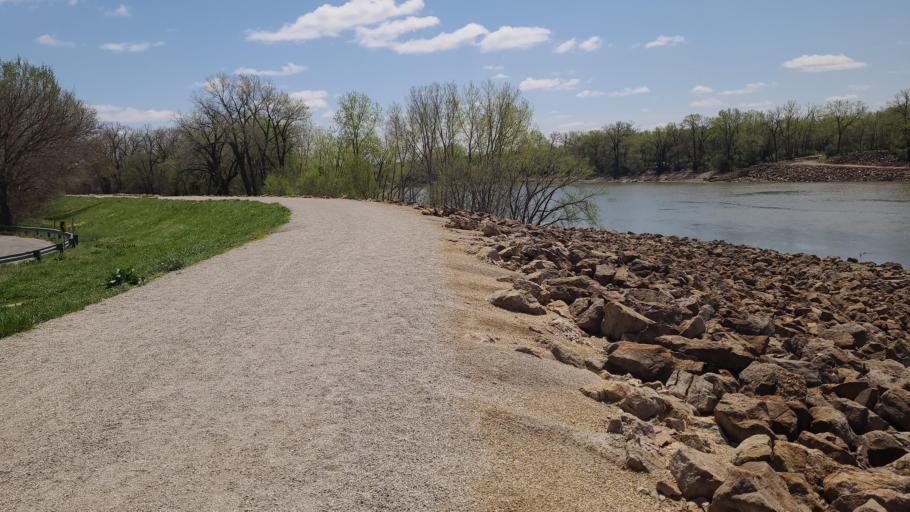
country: US
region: Kansas
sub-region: Douglas County
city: Lawrence
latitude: 38.9753
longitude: -95.2315
